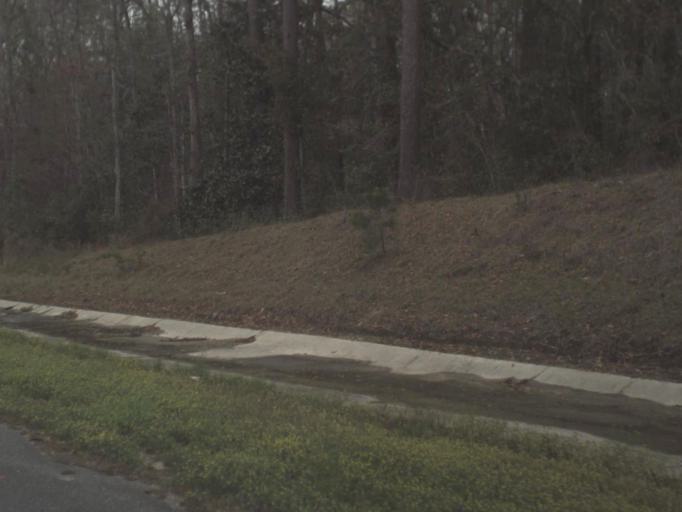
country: US
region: Florida
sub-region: Liberty County
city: Bristol
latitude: 30.3945
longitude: -84.7925
